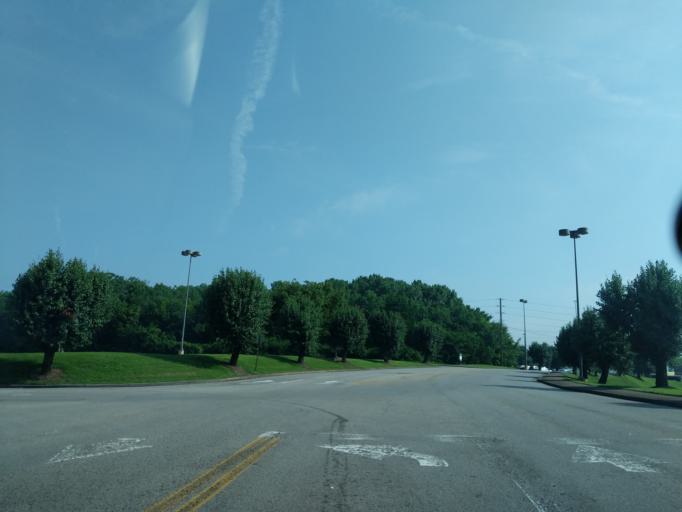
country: US
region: Tennessee
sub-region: Davidson County
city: Goodlettsville
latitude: 36.3045
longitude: -86.6952
